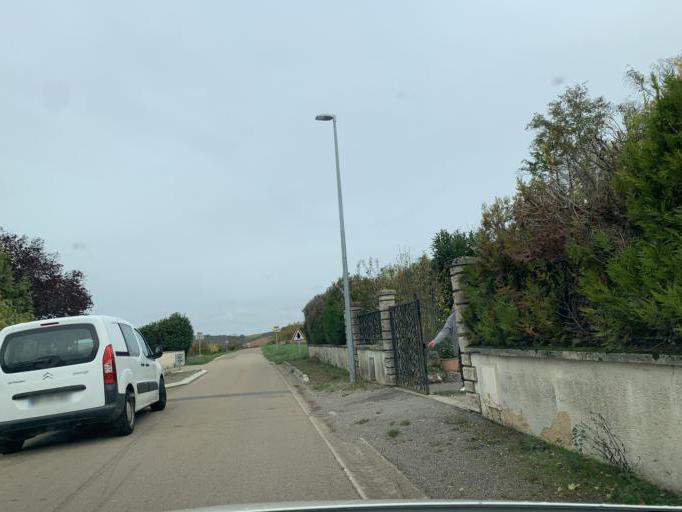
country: FR
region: Bourgogne
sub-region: Departement de l'Yonne
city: Champs-sur-Yonne
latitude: 47.7218
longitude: 3.5883
